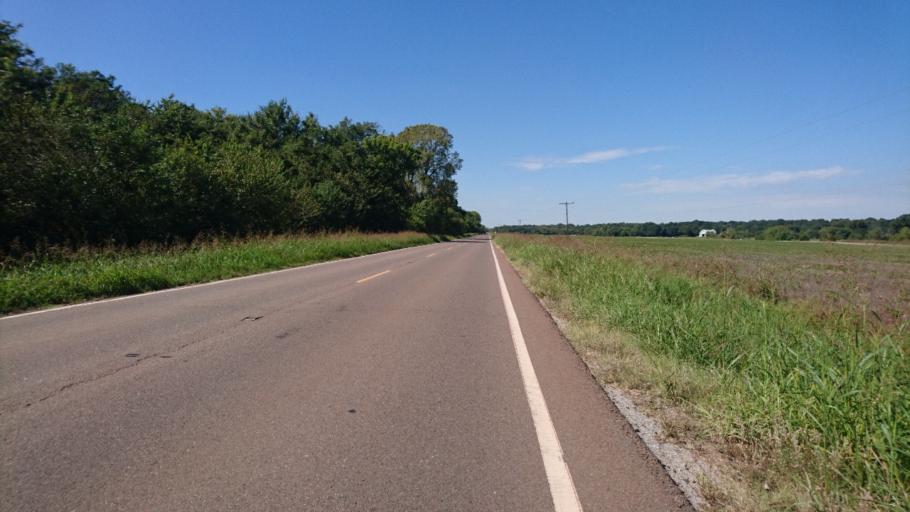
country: US
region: Oklahoma
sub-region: Oklahoma County
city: Luther
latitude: 35.6618
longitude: -97.2579
